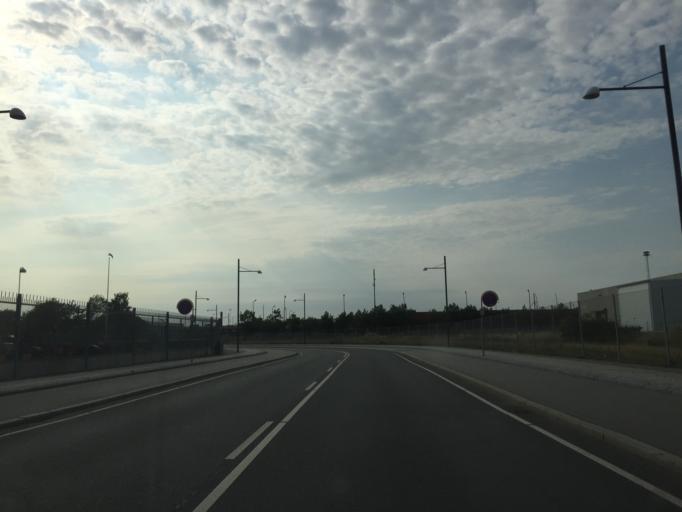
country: DK
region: Capital Region
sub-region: Gentofte Kommune
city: Charlottenlund
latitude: 55.7164
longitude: 12.6082
